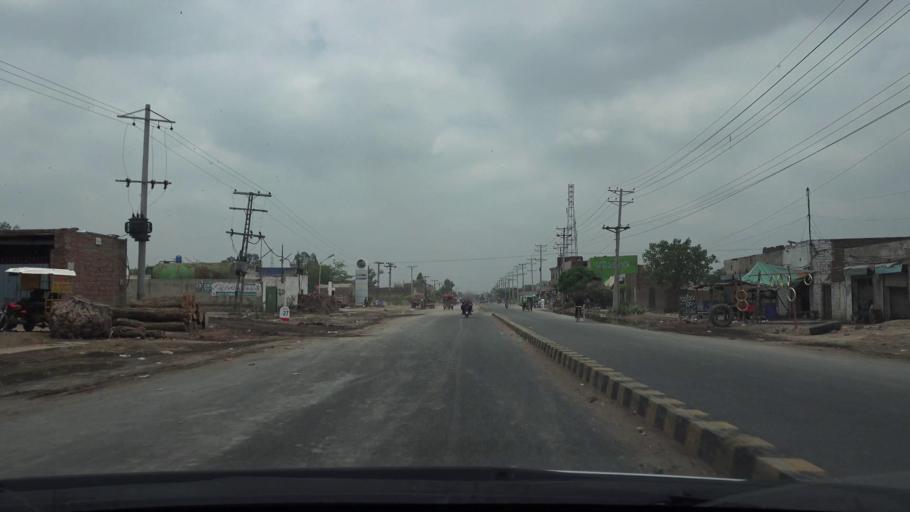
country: PK
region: Punjab
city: Faisalabad
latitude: 31.3927
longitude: 73.1835
